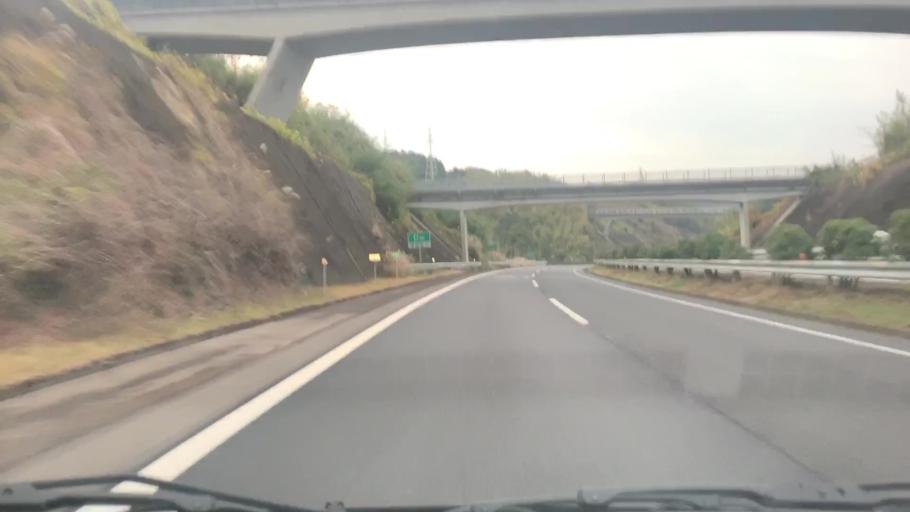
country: JP
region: Nagasaki
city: Omura
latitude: 33.0092
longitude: 129.9531
